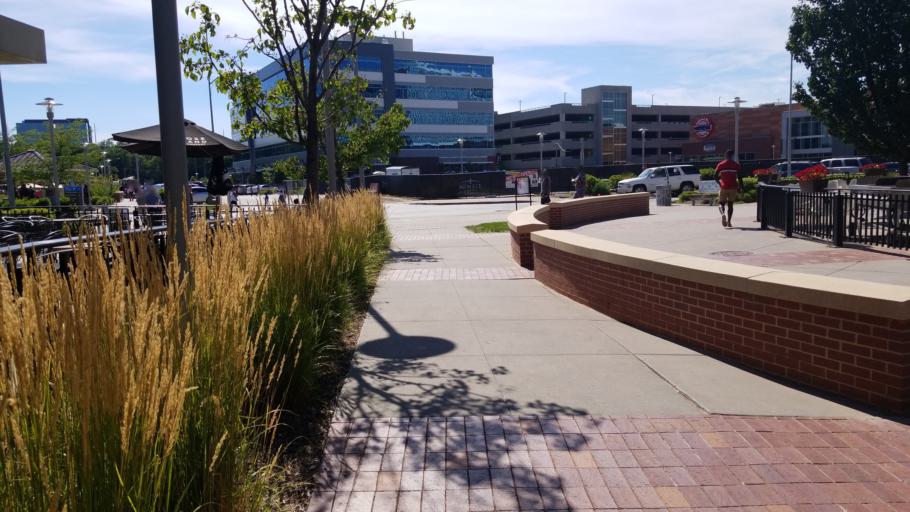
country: US
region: Nebraska
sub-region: Douglas County
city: Ralston
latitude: 41.2389
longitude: -96.0142
